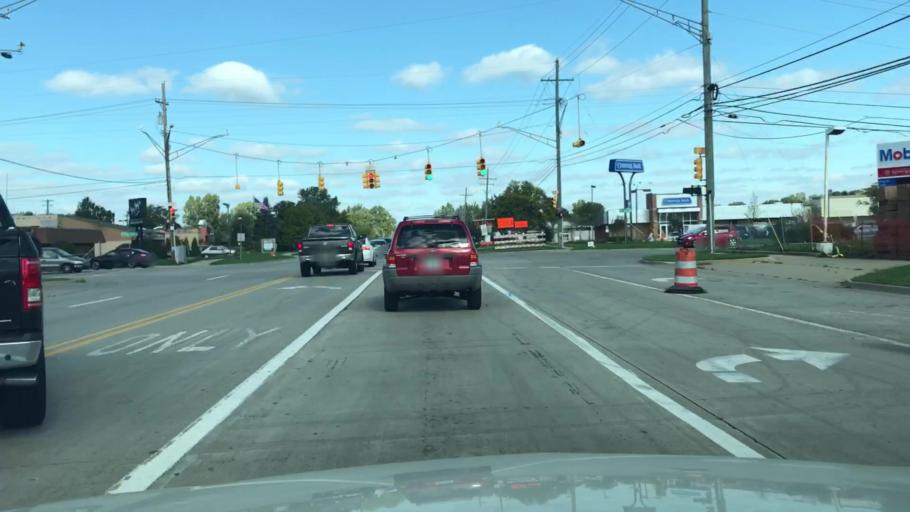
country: US
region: Michigan
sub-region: Macomb County
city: Sterling Heights
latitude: 42.5925
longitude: -83.0899
